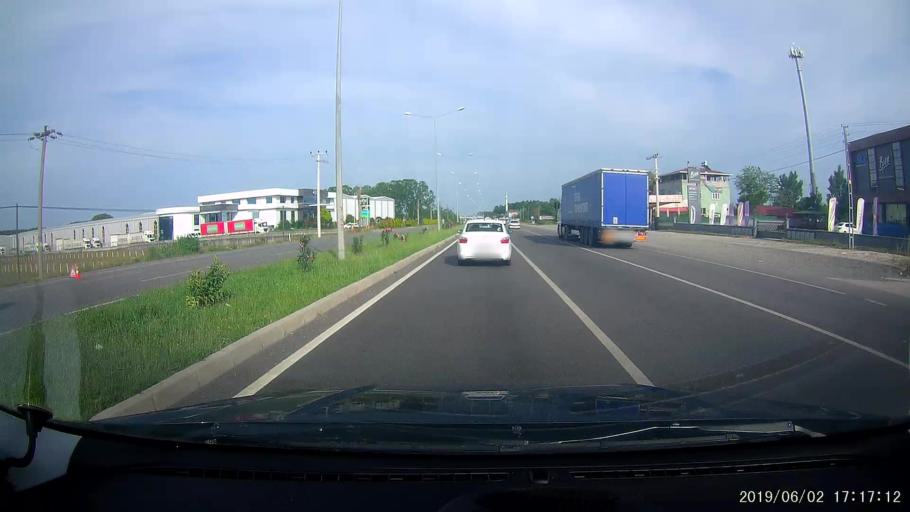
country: TR
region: Samsun
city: Dikbiyik
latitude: 41.2305
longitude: 36.5777
